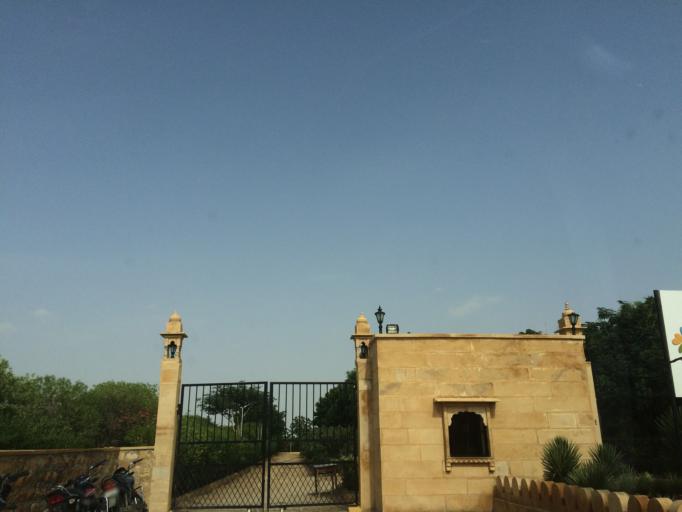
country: IN
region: Rajasthan
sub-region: Jaisalmer
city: Jaisalmer
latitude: 26.8661
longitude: 70.8701
